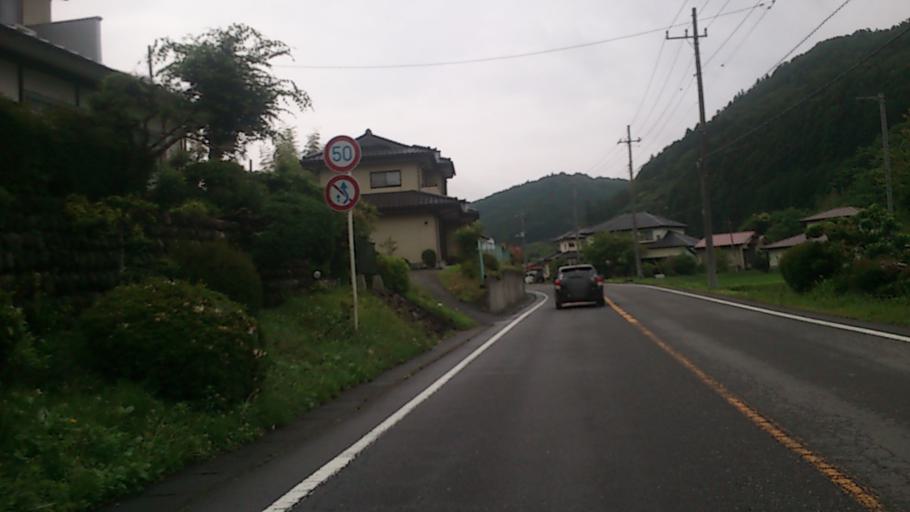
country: JP
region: Tochigi
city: Karasuyama
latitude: 36.7205
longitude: 140.1956
